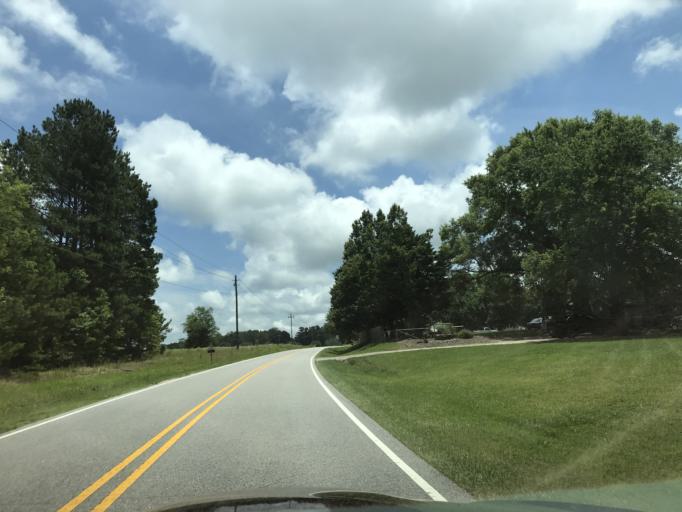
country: US
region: North Carolina
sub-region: Wake County
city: Rolesville
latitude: 35.9569
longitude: -78.3952
